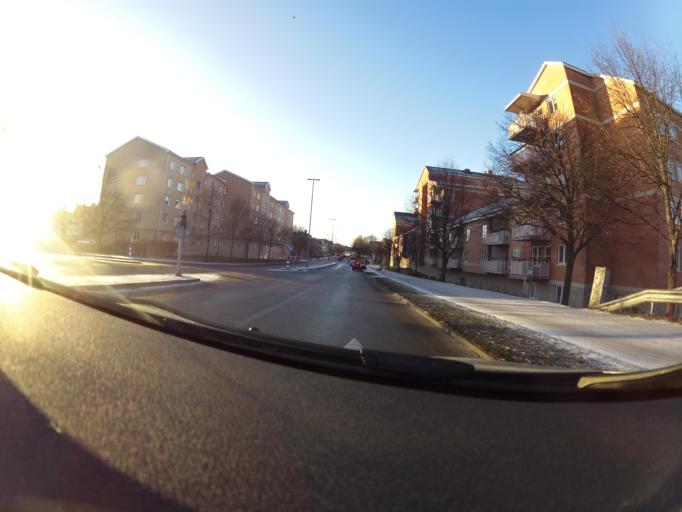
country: SE
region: Gaevleborg
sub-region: Gavle Kommun
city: Gavle
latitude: 60.6692
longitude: 17.1573
